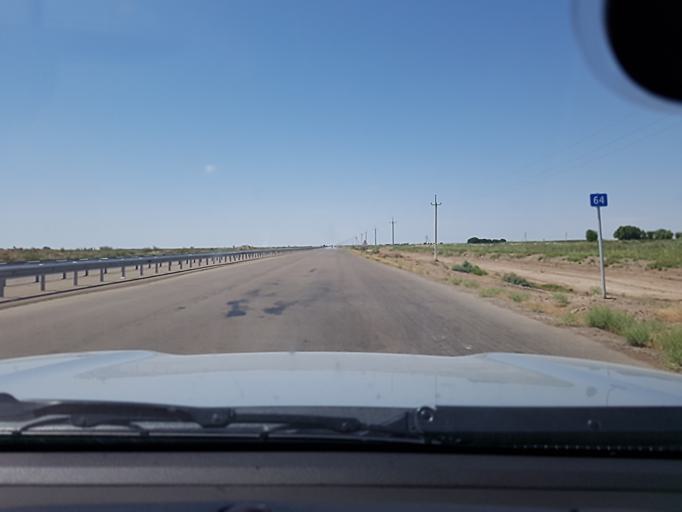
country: TM
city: Akdepe
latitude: 41.7396
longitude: 59.1929
